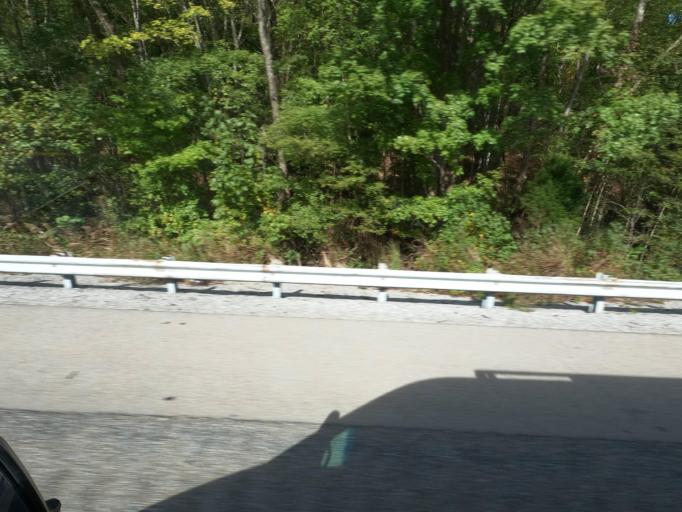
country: US
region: Tennessee
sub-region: Humphreys County
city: New Johnsonville
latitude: 35.8738
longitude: -87.8590
